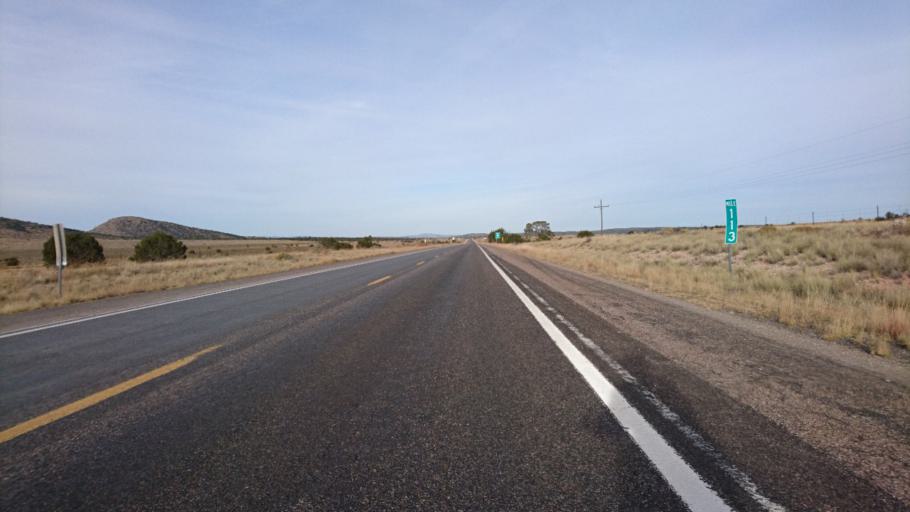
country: US
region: Arizona
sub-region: Mohave County
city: Peach Springs
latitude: 35.5411
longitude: -113.2709
